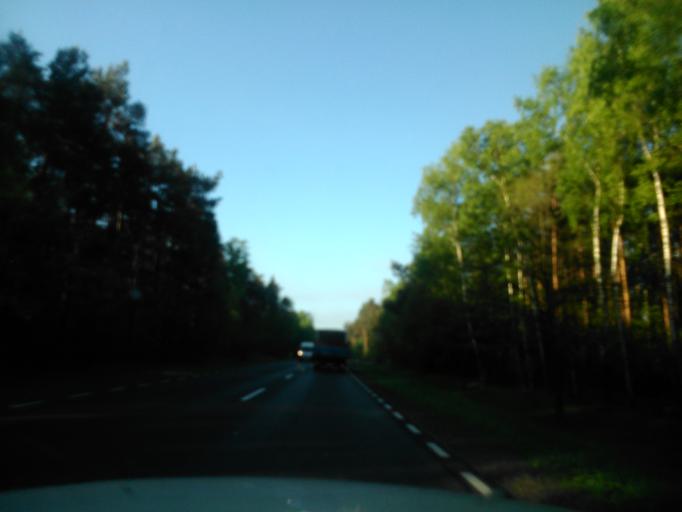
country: PL
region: Masovian Voivodeship
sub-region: Powiat sochaczewski
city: Mlodzieszyn
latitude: 52.3236
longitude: 20.2104
